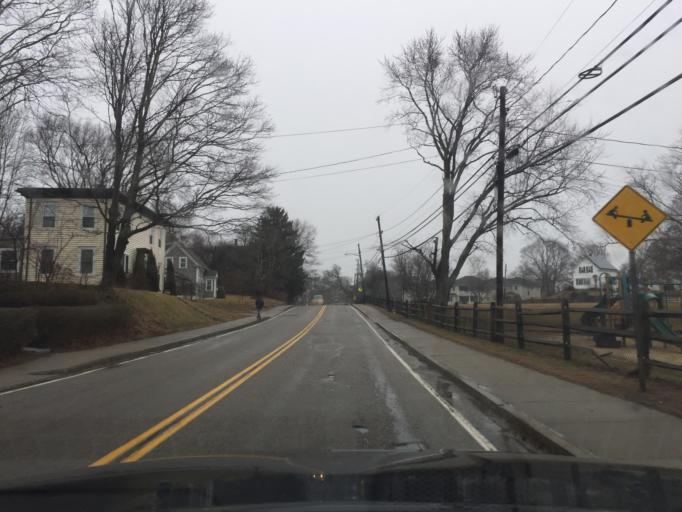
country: US
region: Massachusetts
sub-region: Plymouth County
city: Plymouth
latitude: 41.9472
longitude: -70.6599
